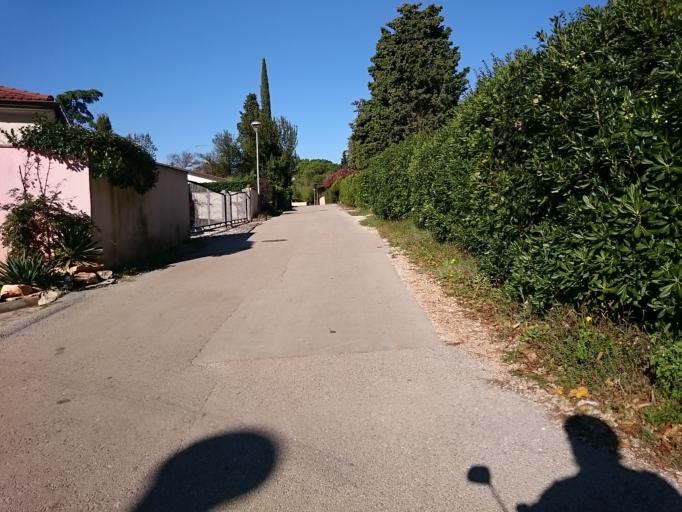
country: HR
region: Istarska
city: Umag
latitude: 45.4037
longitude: 13.5302
